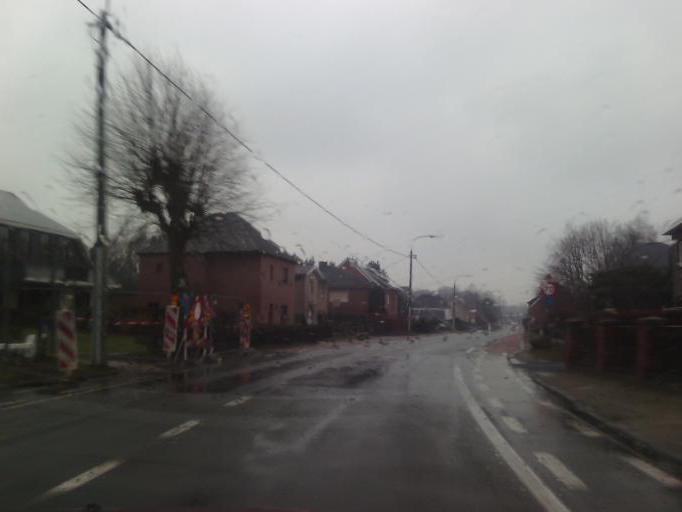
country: BE
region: Flanders
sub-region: Provincie Oost-Vlaanderen
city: Wetteren
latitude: 51.0111
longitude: 3.9124
